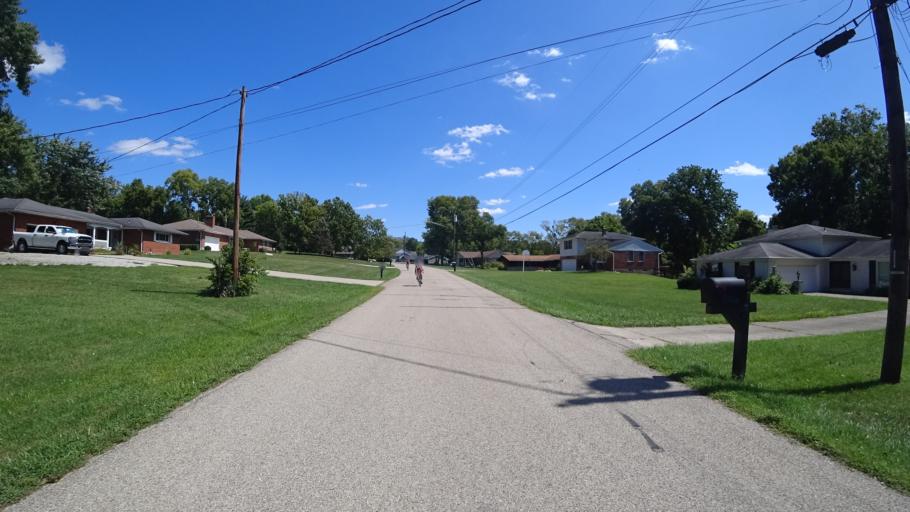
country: US
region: Ohio
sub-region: Butler County
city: New Miami
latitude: 39.4116
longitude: -84.5229
